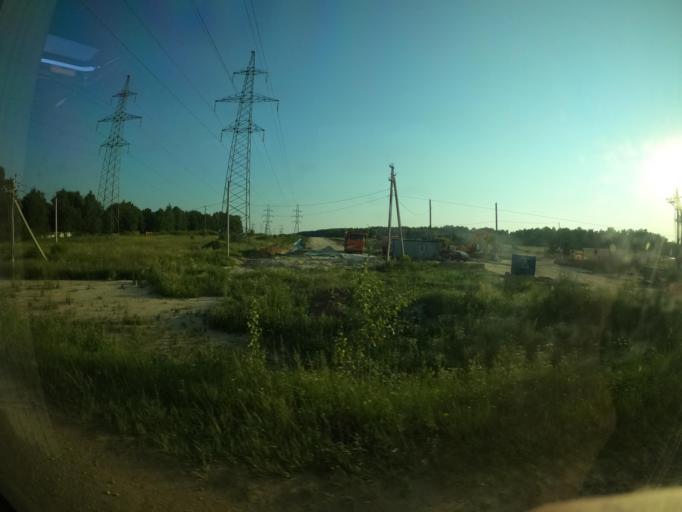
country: RU
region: Moskovskaya
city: Serpukhov
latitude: 54.9488
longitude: 37.3431
